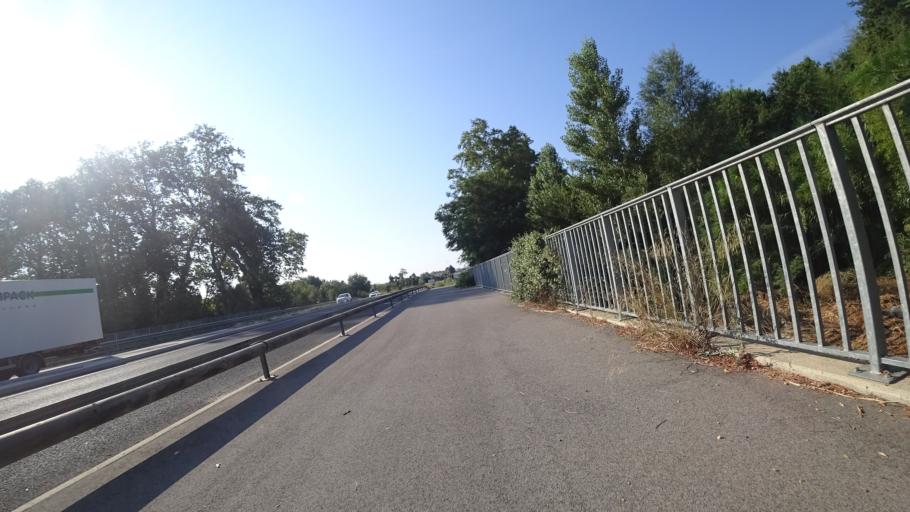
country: FR
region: Languedoc-Roussillon
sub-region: Departement des Pyrenees-Orientales
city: Perpignan
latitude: 42.7152
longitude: 2.9041
